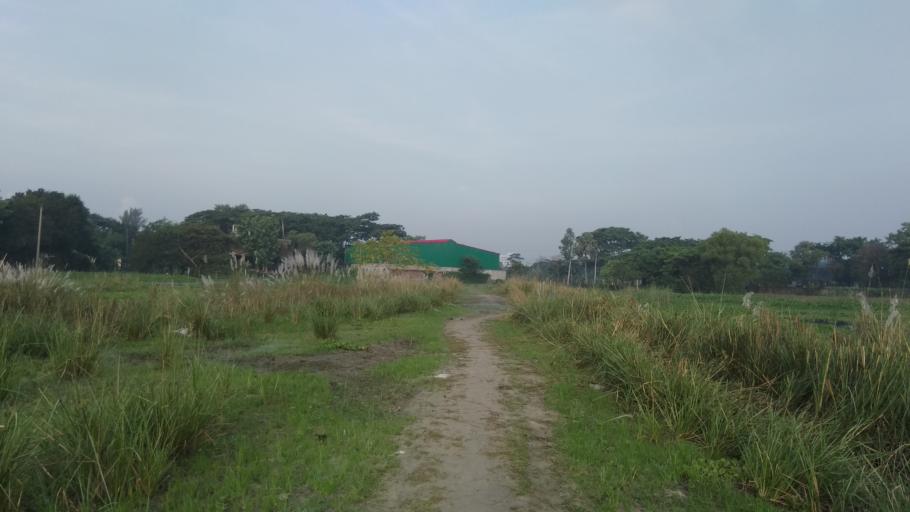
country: BD
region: Dhaka
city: Tungi
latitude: 23.8508
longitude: 90.4416
